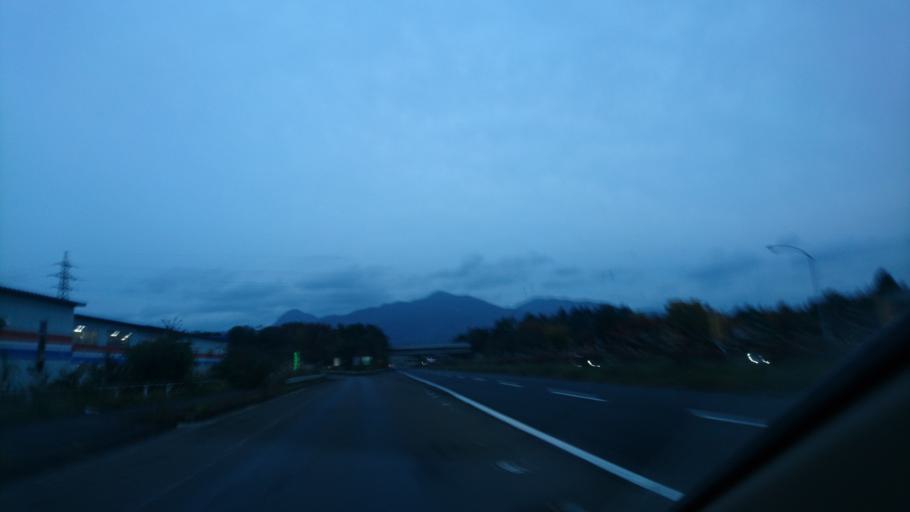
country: JP
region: Iwate
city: Morioka-shi
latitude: 39.6559
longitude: 141.1281
